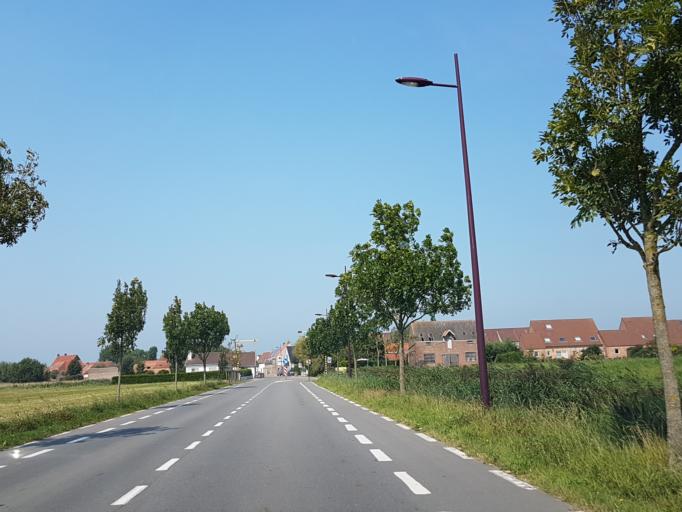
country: BE
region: Flanders
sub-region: Provincie West-Vlaanderen
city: De Haan
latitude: 51.2510
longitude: 3.0586
